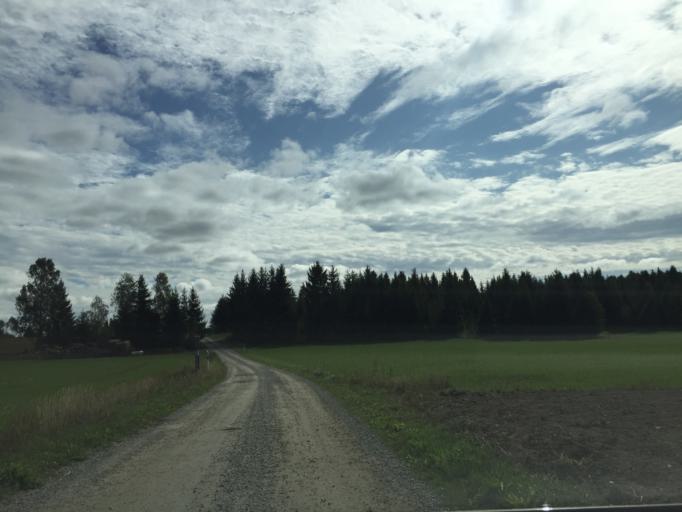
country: NO
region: Ostfold
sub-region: Hobol
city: Elvestad
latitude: 59.6313
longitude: 10.8915
